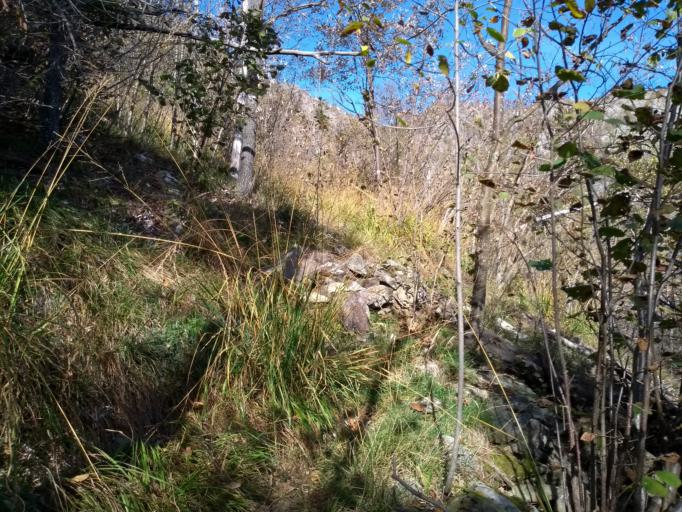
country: IT
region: Piedmont
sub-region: Provincia di Torino
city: La Villa
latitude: 45.2560
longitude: 7.4041
